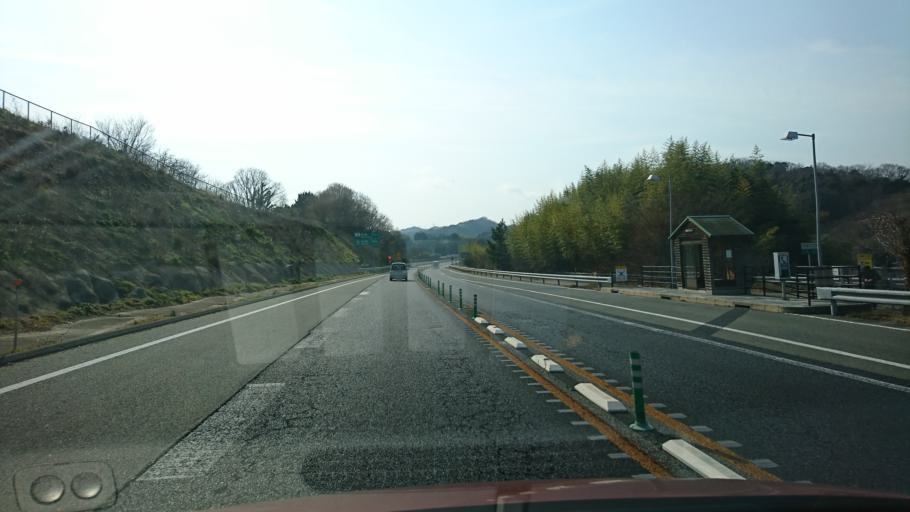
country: JP
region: Hiroshima
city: Onomichi
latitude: 34.3976
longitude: 133.2085
